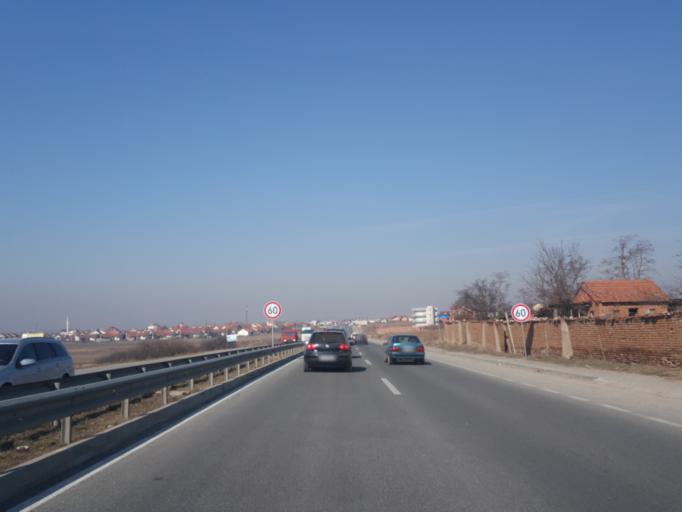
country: XK
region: Pristina
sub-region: Komuna e Obiliqit
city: Obiliq
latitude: 42.7543
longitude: 21.0374
